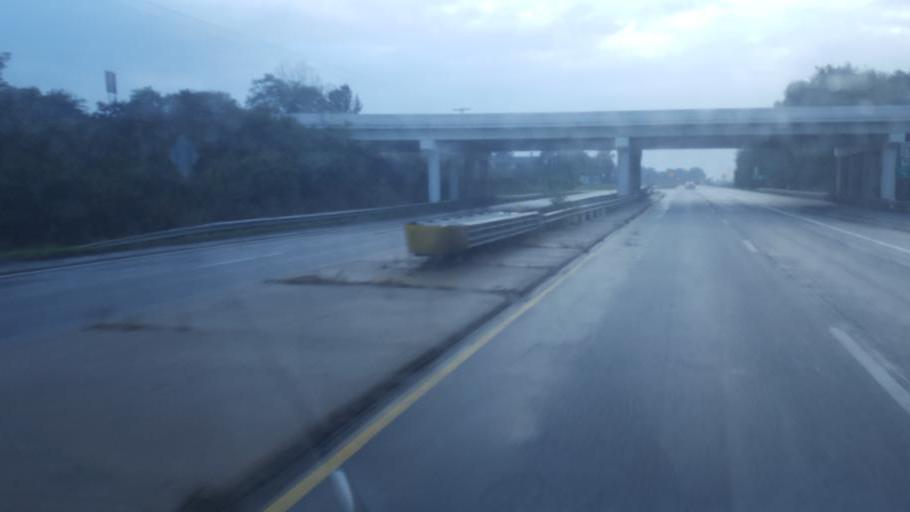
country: US
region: Ohio
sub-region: Wayne County
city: Wooster
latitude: 40.7711
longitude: -81.9150
